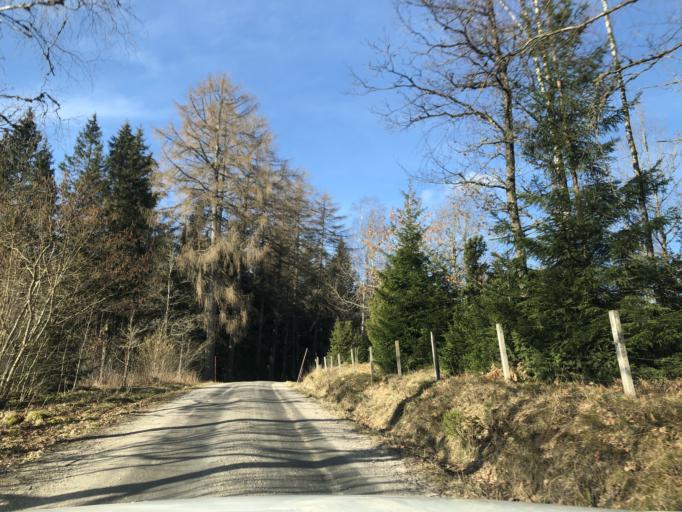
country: SE
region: Vaestra Goetaland
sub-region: Ulricehamns Kommun
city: Ulricehamn
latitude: 57.8071
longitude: 13.3883
